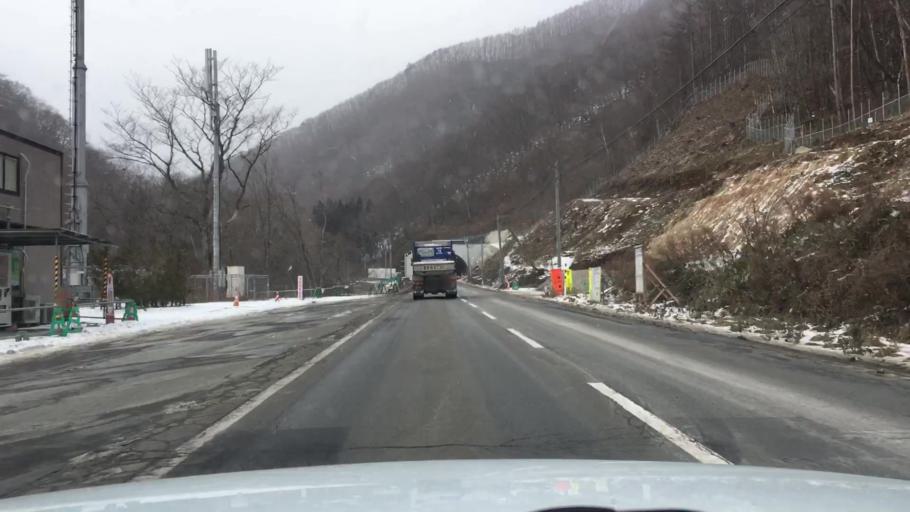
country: JP
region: Iwate
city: Tono
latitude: 39.6245
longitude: 141.4705
